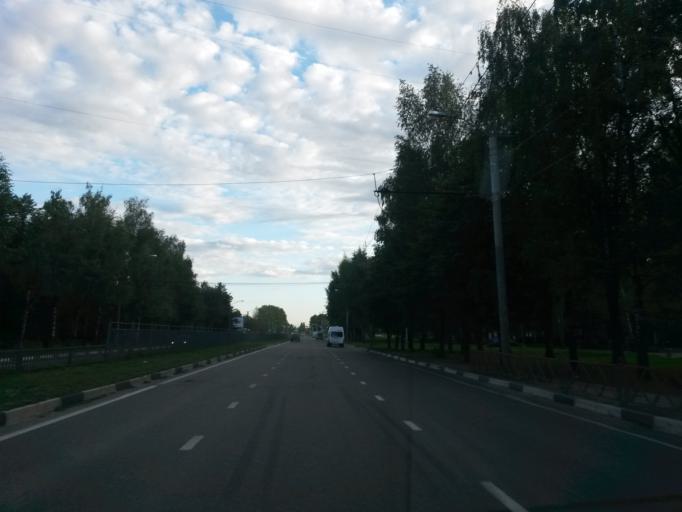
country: RU
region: Jaroslavl
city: Yaroslavl
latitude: 57.6773
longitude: 39.7763
